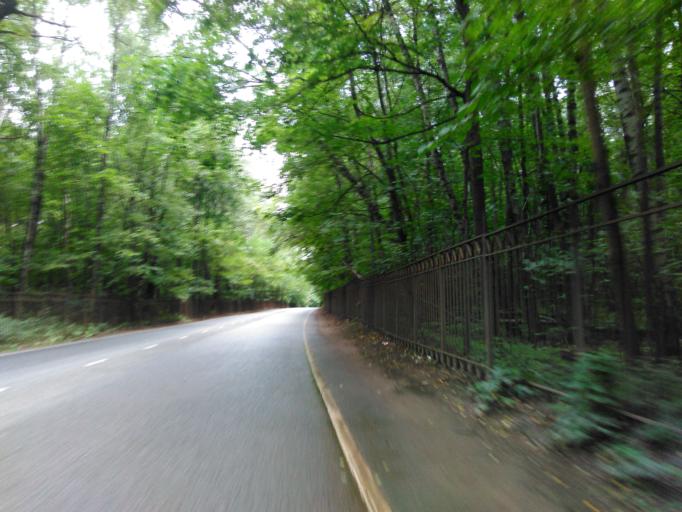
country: RU
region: Moscow
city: Rostokino
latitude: 55.8286
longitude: 37.6921
